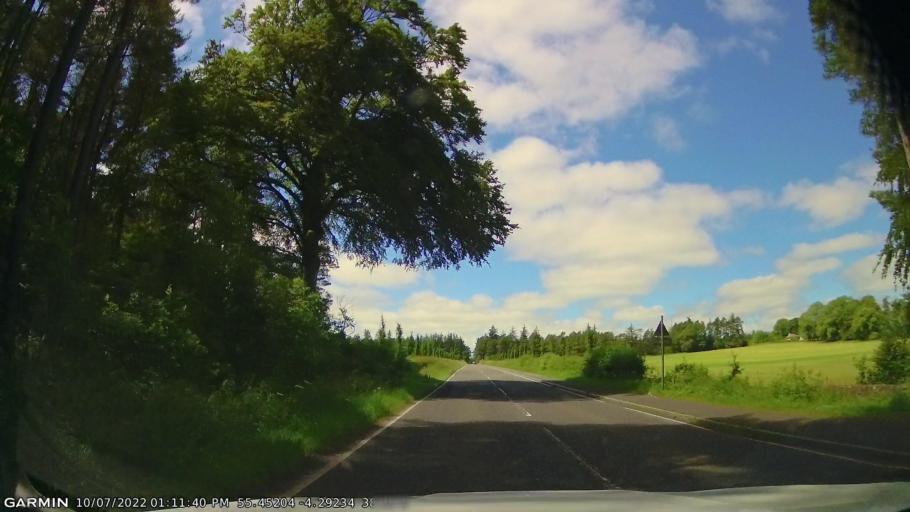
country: GB
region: Scotland
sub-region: East Ayrshire
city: Auchinleck
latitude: 55.4521
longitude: -4.2924
